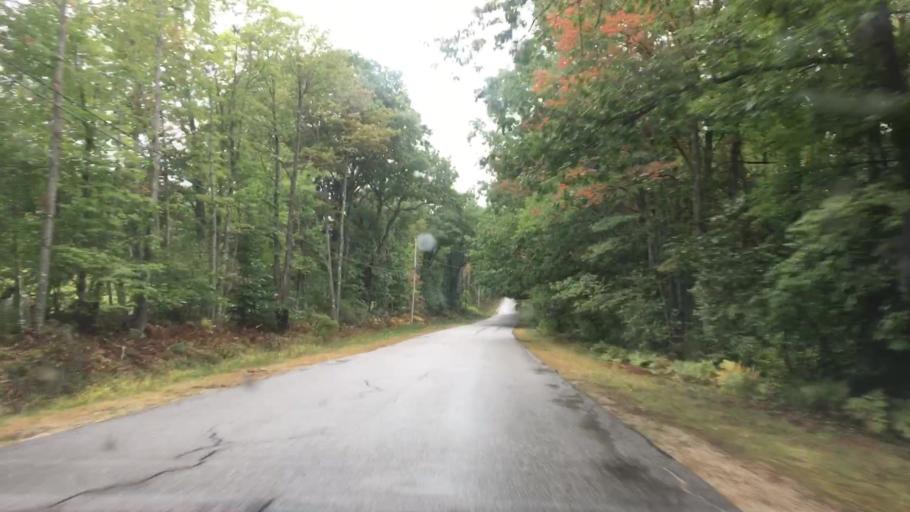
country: US
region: Maine
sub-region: Cumberland County
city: Harrison
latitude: 44.0551
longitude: -70.6190
